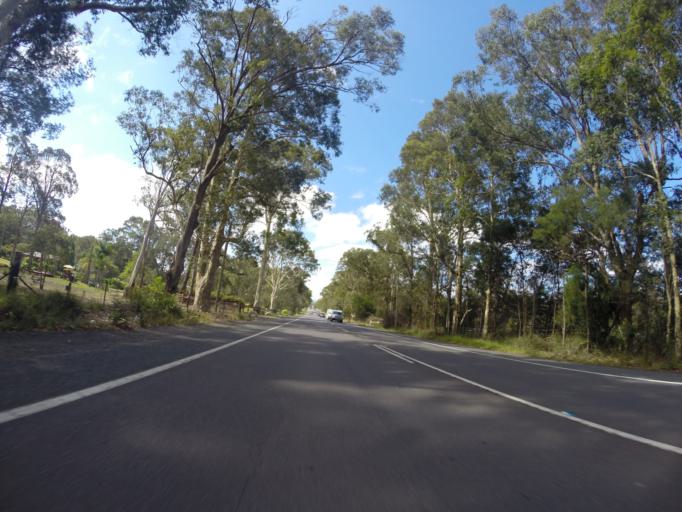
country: AU
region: New South Wales
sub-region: Shoalhaven Shire
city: Falls Creek
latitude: -34.9989
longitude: 150.5838
